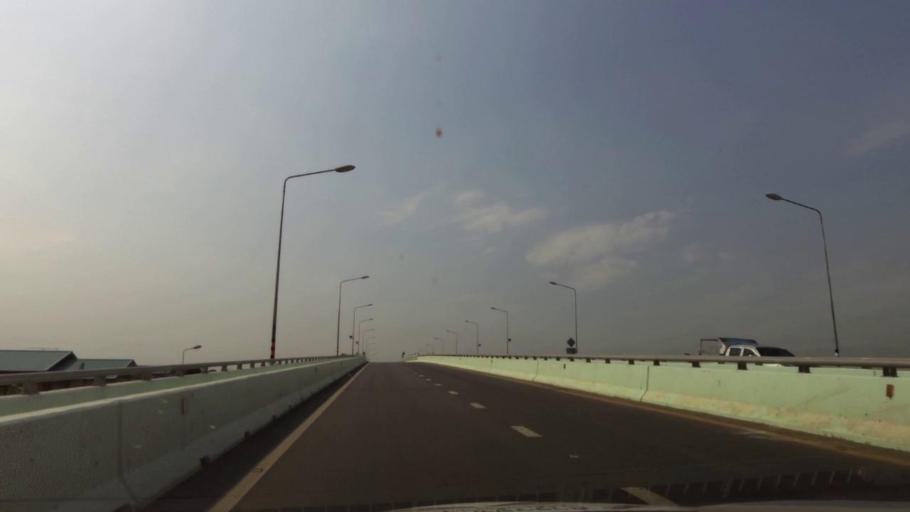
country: TH
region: Phra Nakhon Si Ayutthaya
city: Phra Nakhon Si Ayutthaya
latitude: 14.3302
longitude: 100.5773
